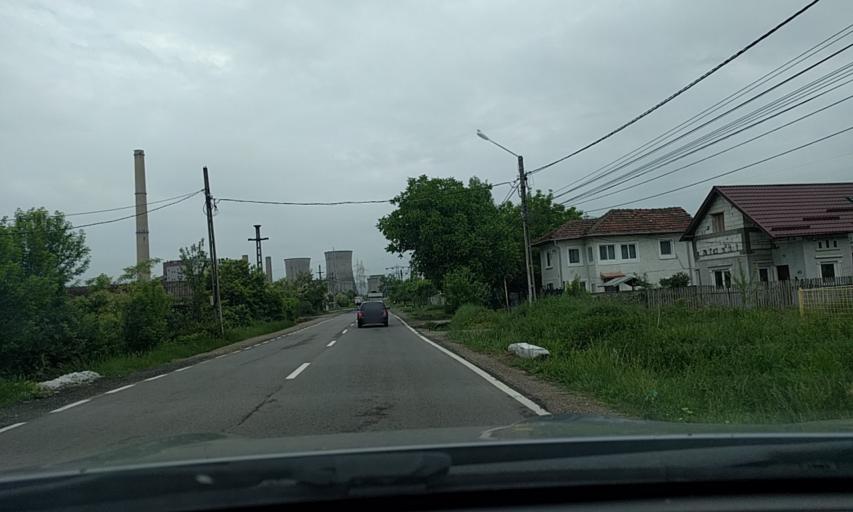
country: RO
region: Dambovita
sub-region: Comuna Doicesti
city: Doicesti
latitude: 44.9955
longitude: 25.4041
